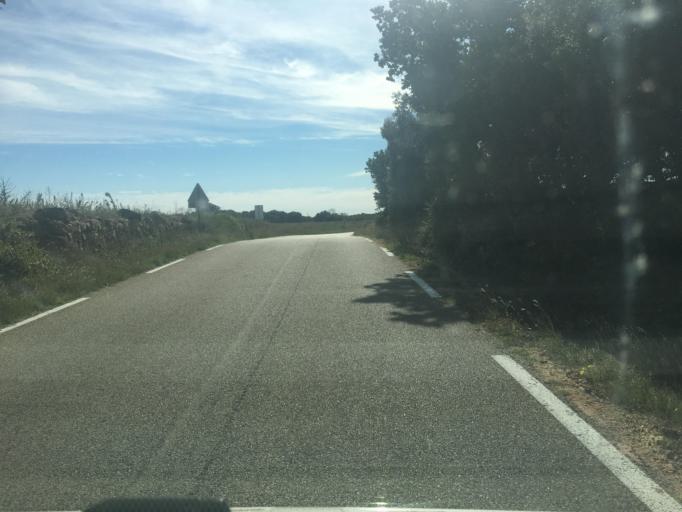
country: FR
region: Languedoc-Roussillon
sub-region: Departement du Gard
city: Connaux
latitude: 44.0373
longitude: 4.5446
